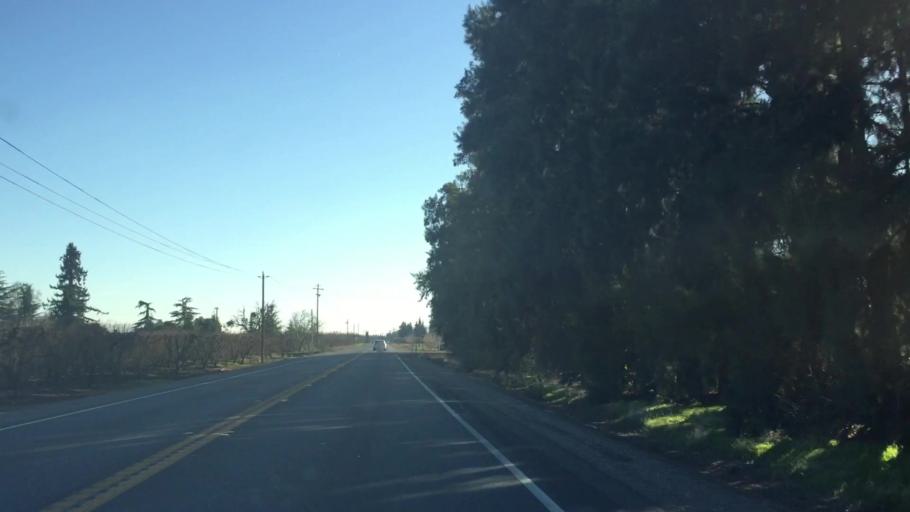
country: US
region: California
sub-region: Sutter County
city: Live Oak
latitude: 39.3030
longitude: -121.5953
